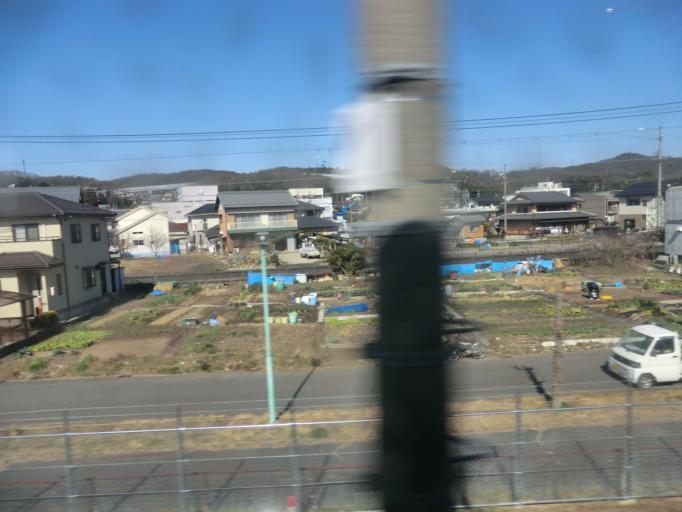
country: JP
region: Gifu
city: Toki
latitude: 35.3571
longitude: 137.1775
